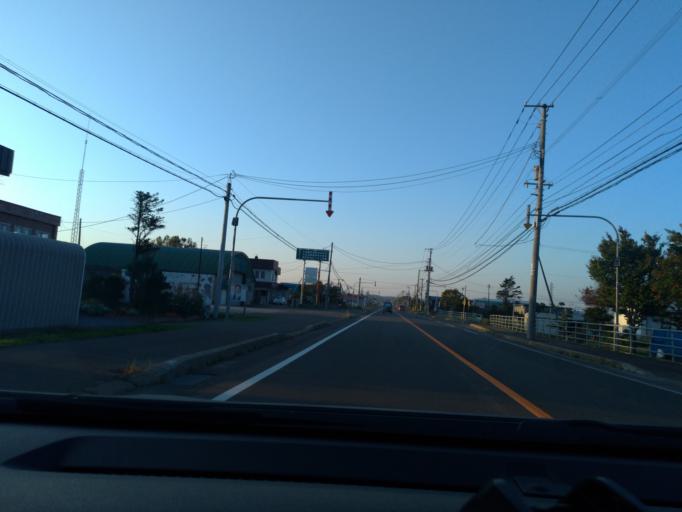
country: JP
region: Hokkaido
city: Tobetsu
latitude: 43.2038
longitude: 141.5207
